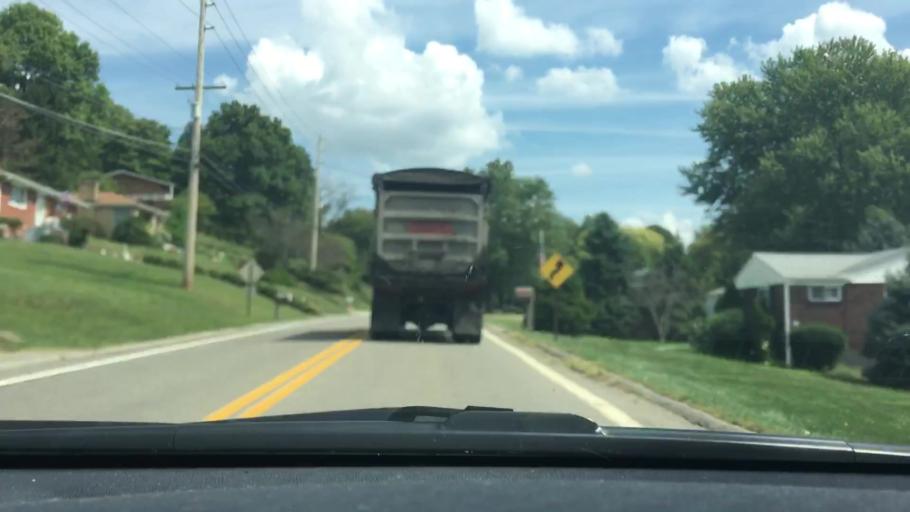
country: US
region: Pennsylvania
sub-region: Washington County
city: Gastonville
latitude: 40.2502
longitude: -79.9548
